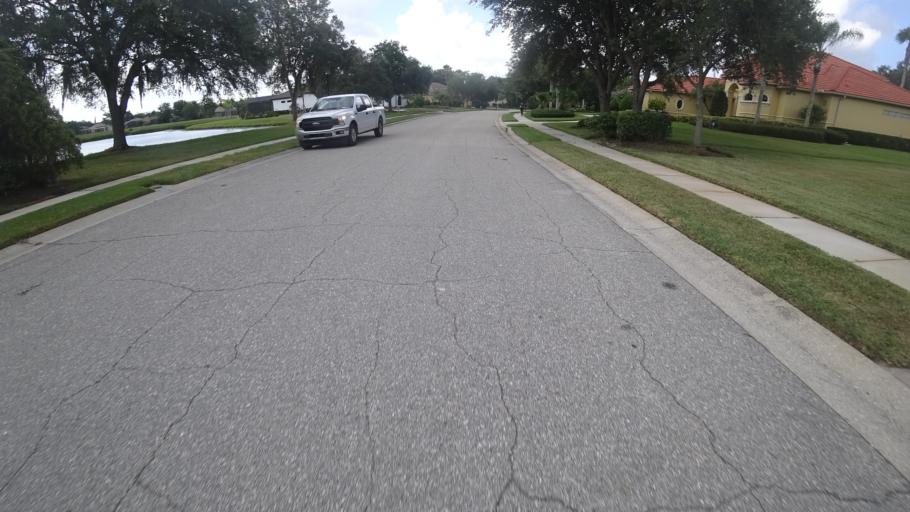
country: US
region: Florida
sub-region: Sarasota County
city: The Meadows
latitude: 27.4150
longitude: -82.4340
